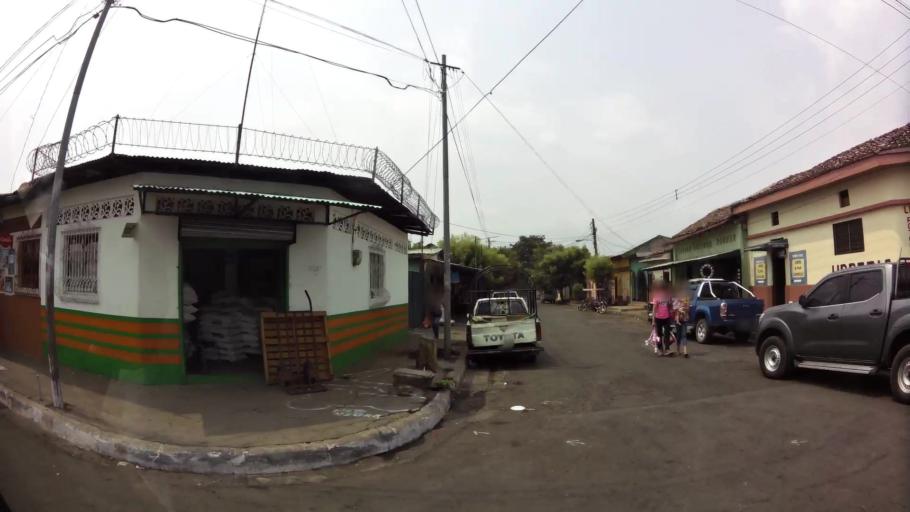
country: NI
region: Chinandega
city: Chinandega
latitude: 12.6336
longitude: -87.1342
